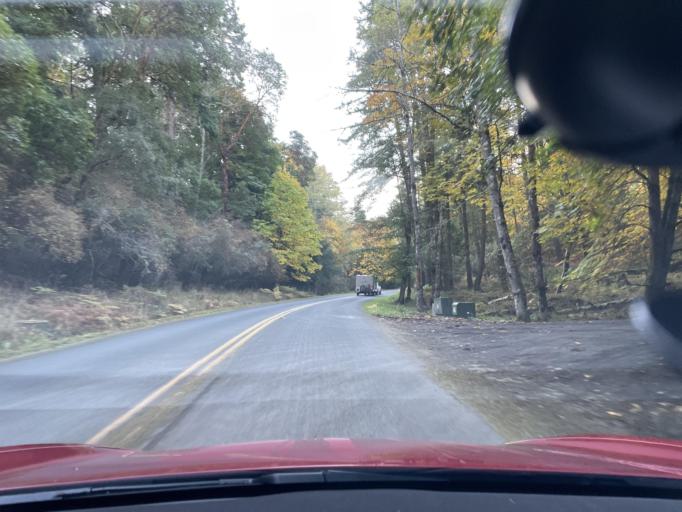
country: US
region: Washington
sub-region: San Juan County
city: Friday Harbor
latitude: 48.5374
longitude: -123.1581
